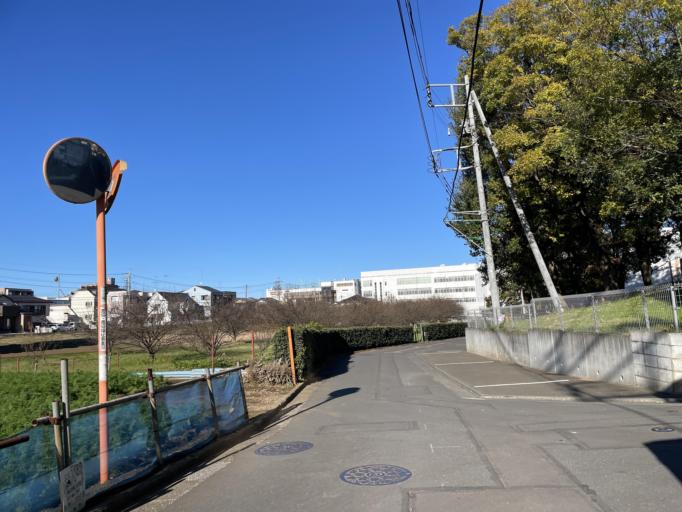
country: JP
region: Saitama
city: Asaka
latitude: 35.8066
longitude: 139.5790
